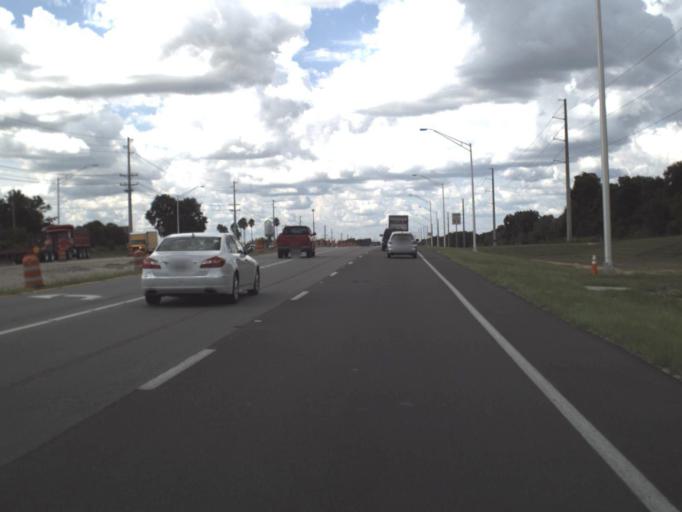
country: US
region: Florida
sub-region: Polk County
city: Highland City
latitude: 27.9773
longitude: -81.8861
